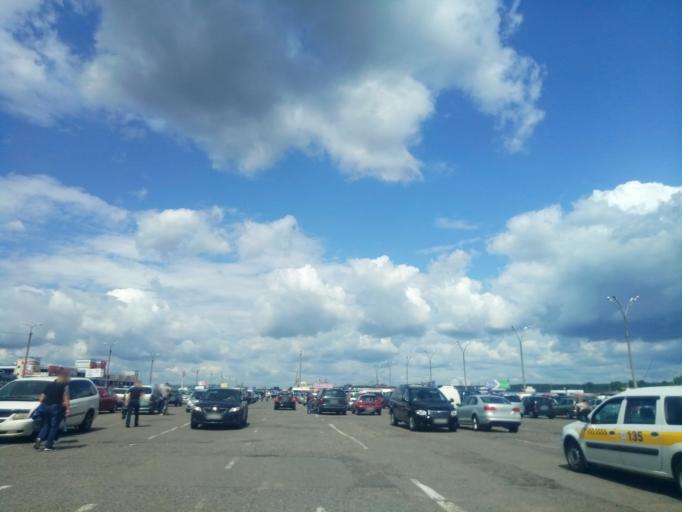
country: BY
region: Minsk
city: Zhdanovichy
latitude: 53.9373
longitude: 27.4499
